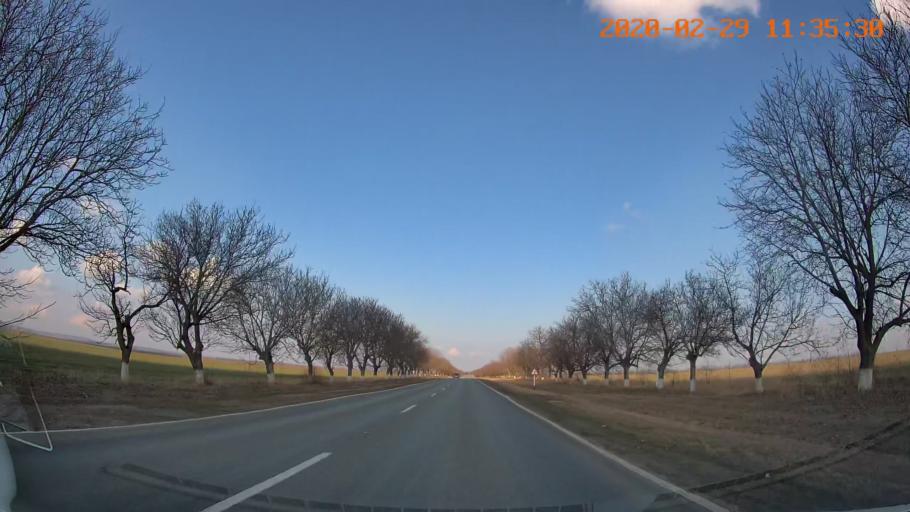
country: MD
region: Rezina
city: Saharna
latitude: 47.5814
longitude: 29.0630
